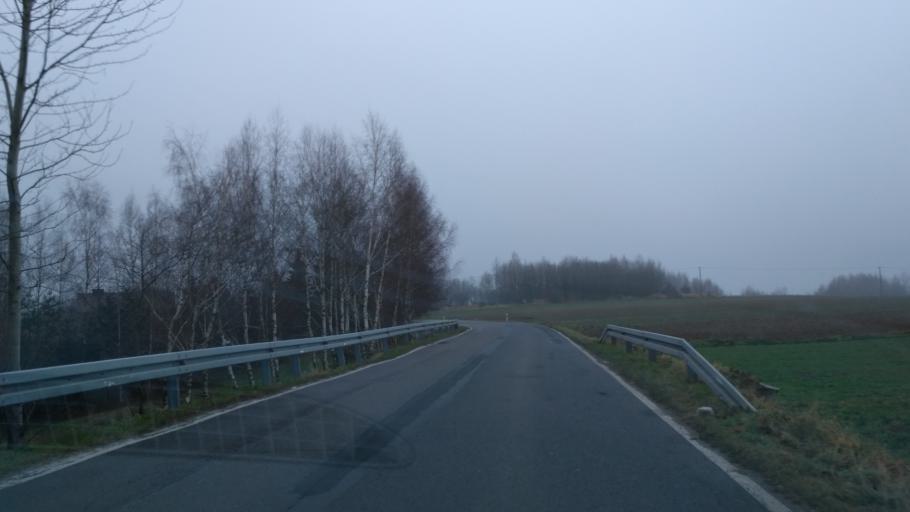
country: PL
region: Subcarpathian Voivodeship
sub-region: Powiat lancucki
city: Handzlowka
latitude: 49.9663
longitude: 22.1914
